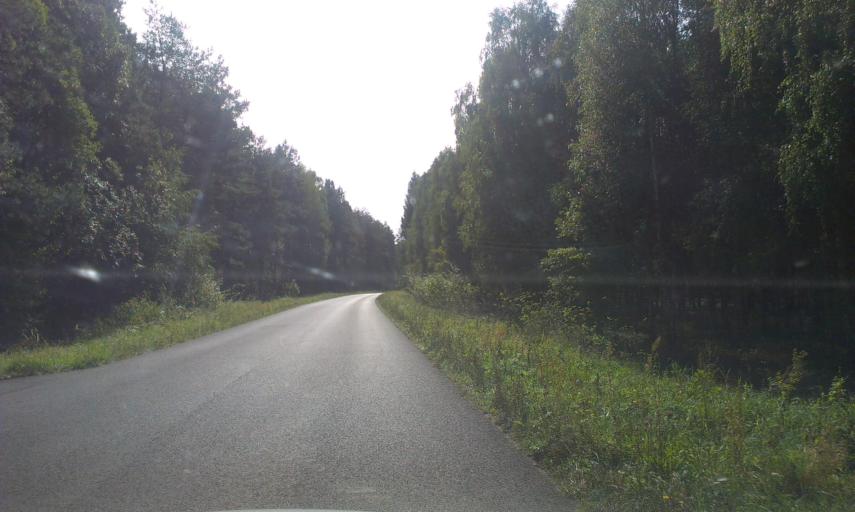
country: PL
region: Greater Poland Voivodeship
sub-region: Powiat zlotowski
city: Zlotow
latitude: 53.4825
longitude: 16.9926
